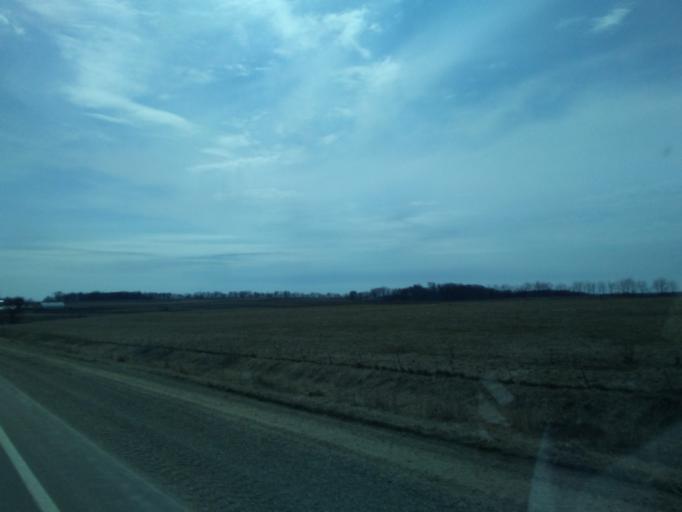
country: US
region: Iowa
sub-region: Winneshiek County
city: Decorah
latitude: 43.4198
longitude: -91.8593
